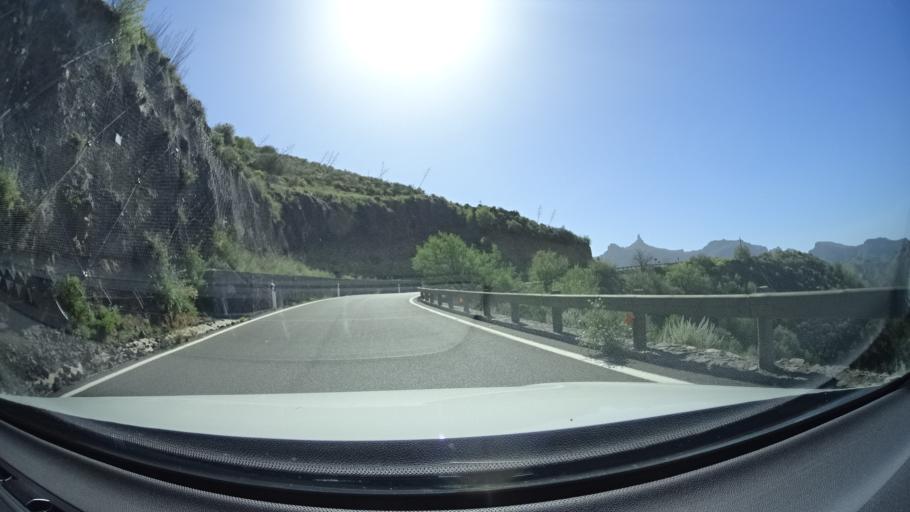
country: ES
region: Canary Islands
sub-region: Provincia de Las Palmas
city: Tejeda
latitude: 28.0117
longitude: -15.6237
